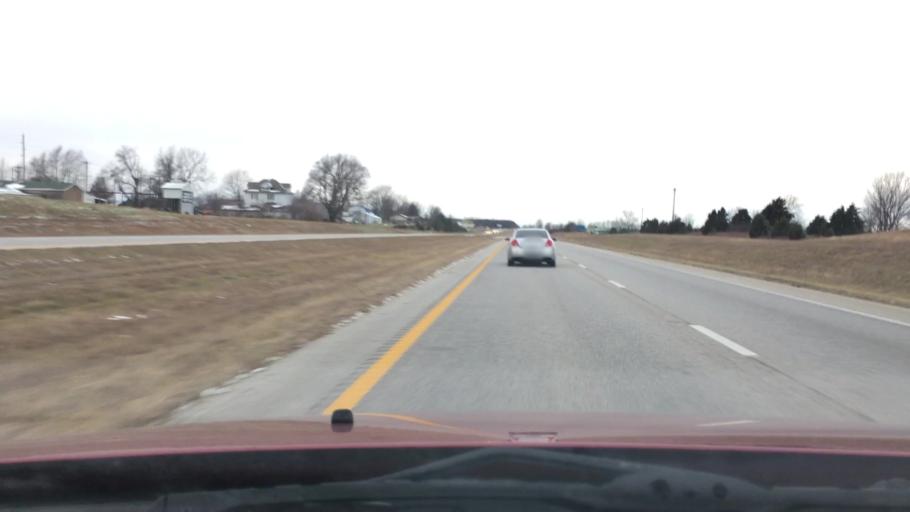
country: US
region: Missouri
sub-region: Webster County
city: Seymour
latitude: 37.1565
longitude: -92.7693
